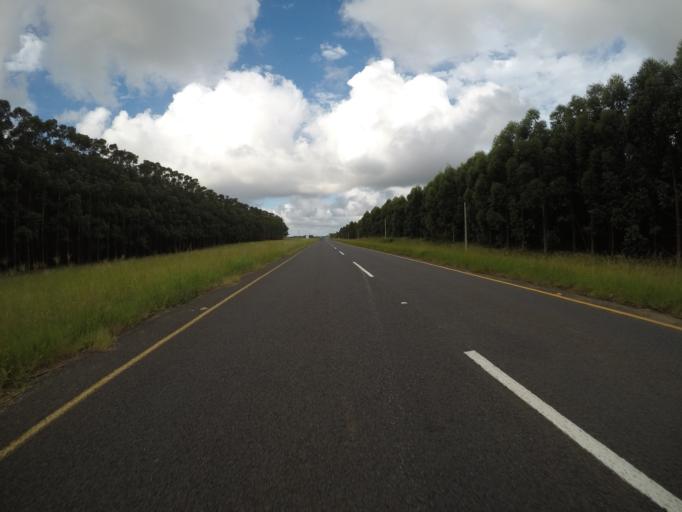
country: ZA
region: KwaZulu-Natal
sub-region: uMkhanyakude District Municipality
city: Mtubatuba
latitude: -28.3880
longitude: 32.2323
